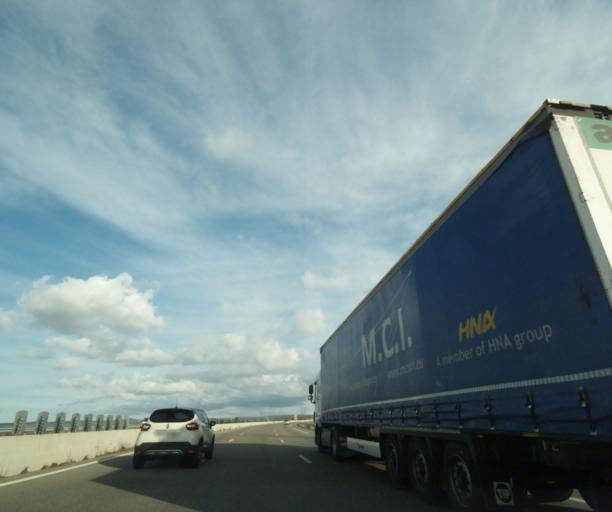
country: FR
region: Provence-Alpes-Cote d'Azur
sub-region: Departement des Bouches-du-Rhone
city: Trets
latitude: 43.4765
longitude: 5.7057
